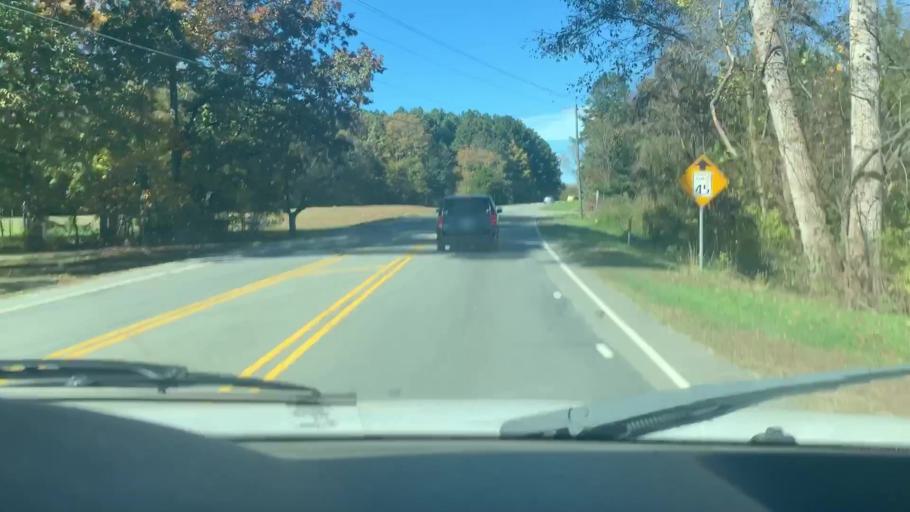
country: US
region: North Carolina
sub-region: Lincoln County
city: Lowesville
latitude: 35.4389
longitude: -80.9788
